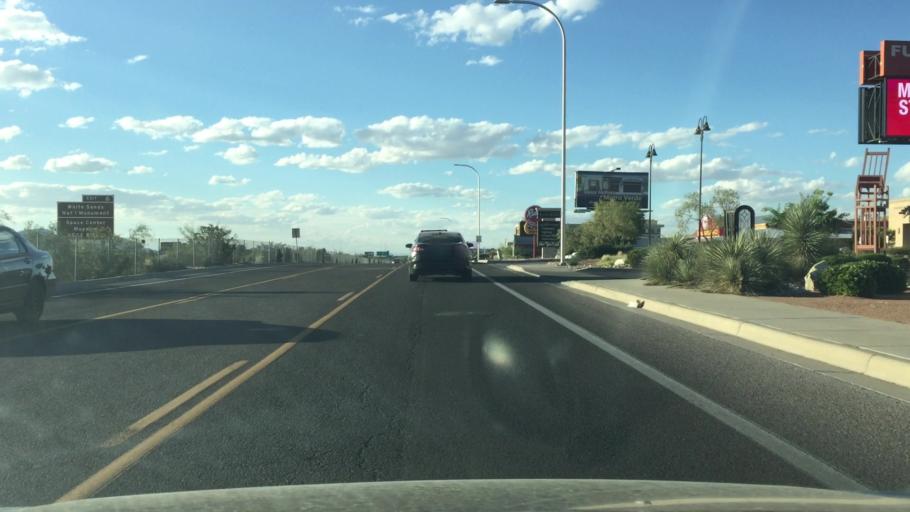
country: US
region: New Mexico
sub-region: Dona Ana County
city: Las Cruces
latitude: 32.3328
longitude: -106.7584
